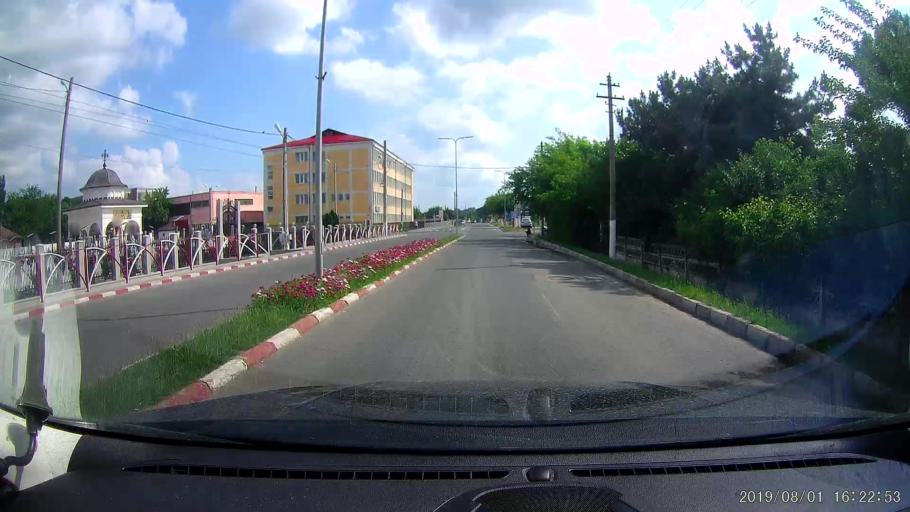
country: RO
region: Calarasi
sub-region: Municipiul Calarasi
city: Calarasi
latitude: 44.2007
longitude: 27.3368
